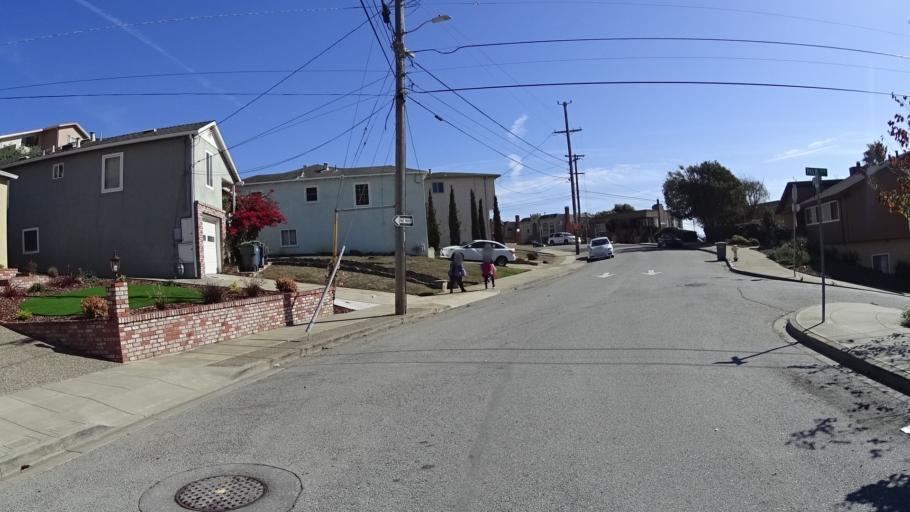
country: US
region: California
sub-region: San Mateo County
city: South San Francisco
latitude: 37.6610
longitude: -122.4169
